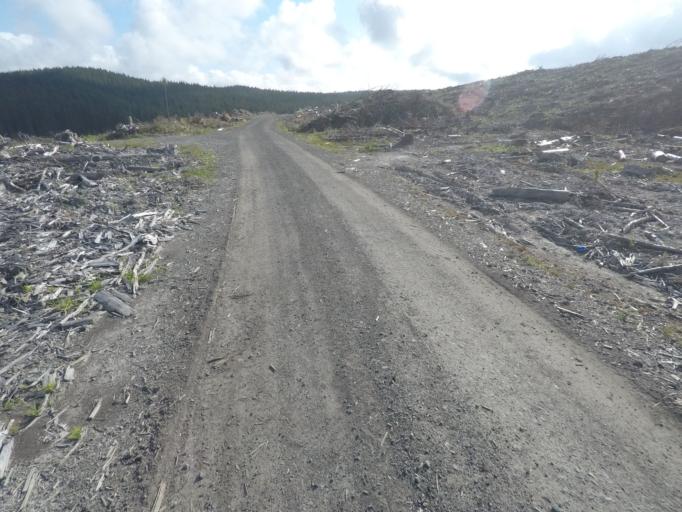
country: NZ
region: Auckland
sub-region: Auckland
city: Parakai
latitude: -36.7143
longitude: 174.5671
